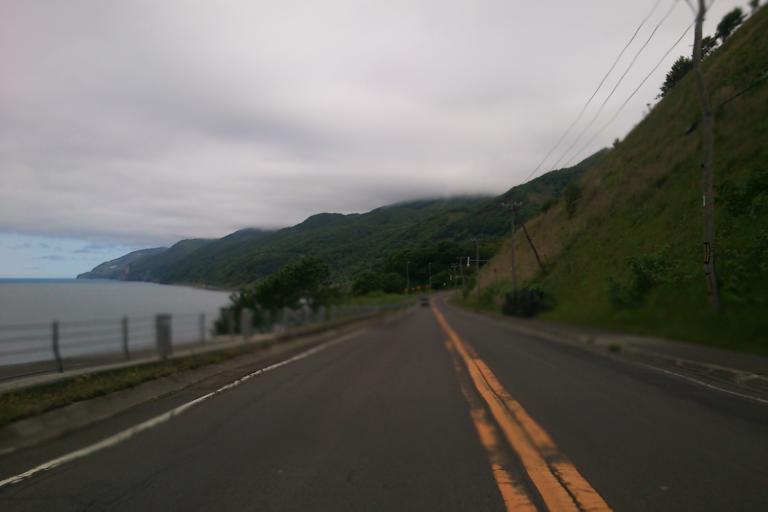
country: JP
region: Hokkaido
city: Ishikari
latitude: 43.4081
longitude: 141.4303
